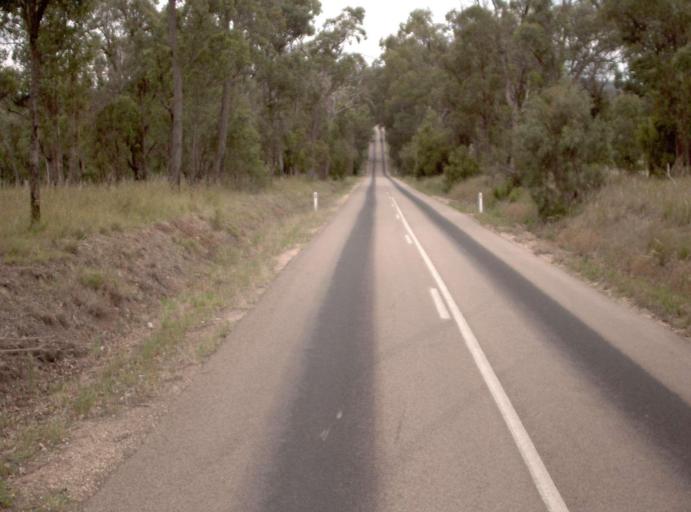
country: AU
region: Victoria
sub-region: East Gippsland
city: Bairnsdale
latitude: -37.7604
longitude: 147.5983
